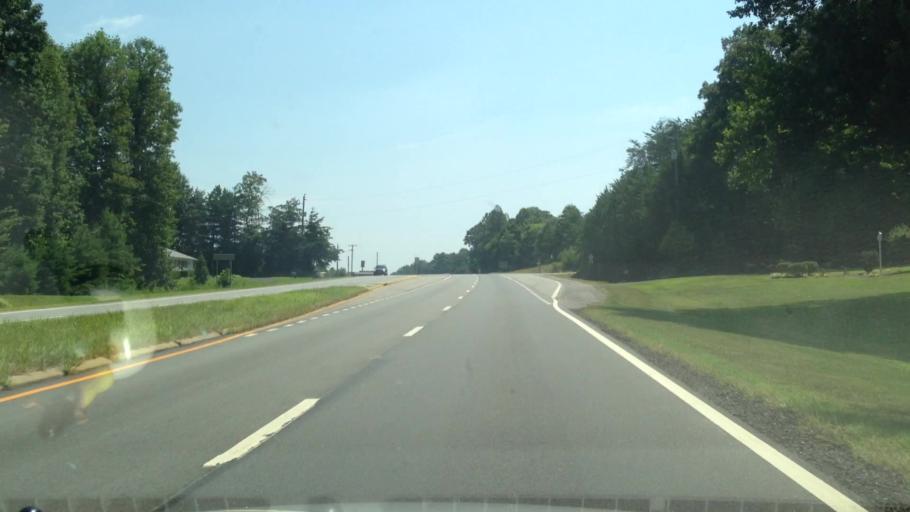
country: US
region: Virginia
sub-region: Patrick County
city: Patrick Springs
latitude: 36.5928
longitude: -80.0956
